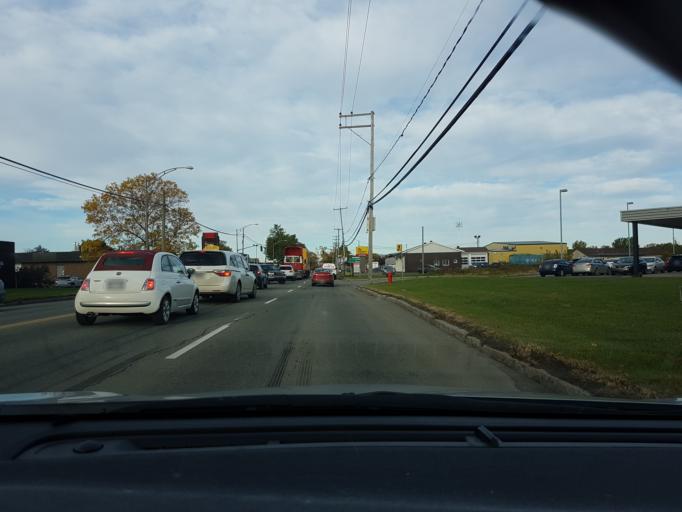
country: CA
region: Quebec
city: L'Ancienne-Lorette
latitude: 46.8065
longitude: -71.2972
